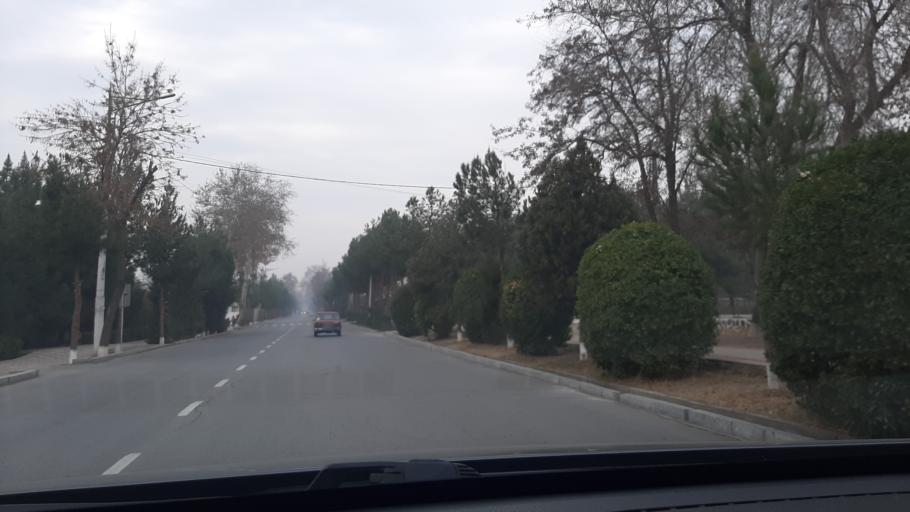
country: TJ
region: Viloyati Sughd
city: Palos
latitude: 40.2643
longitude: 69.7937
